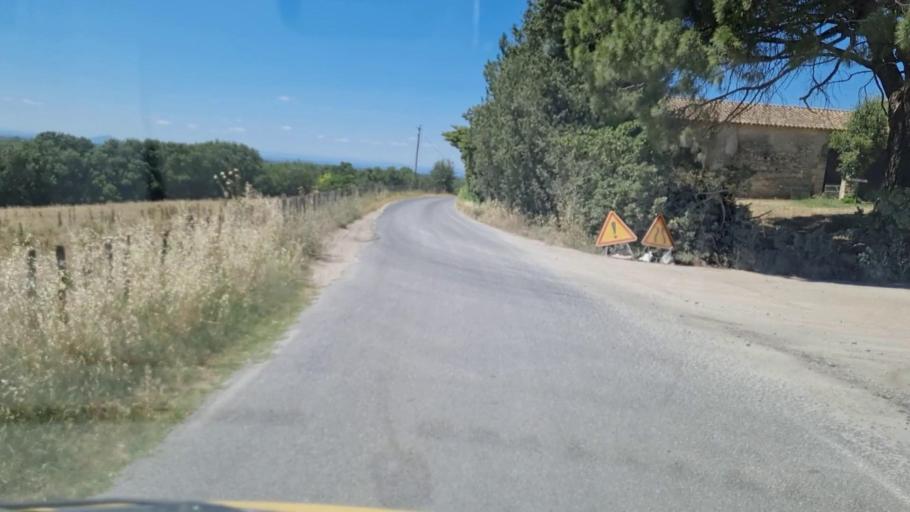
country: FR
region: Languedoc-Roussillon
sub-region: Departement du Gard
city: Le Cailar
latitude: 43.6401
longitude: 4.2540
